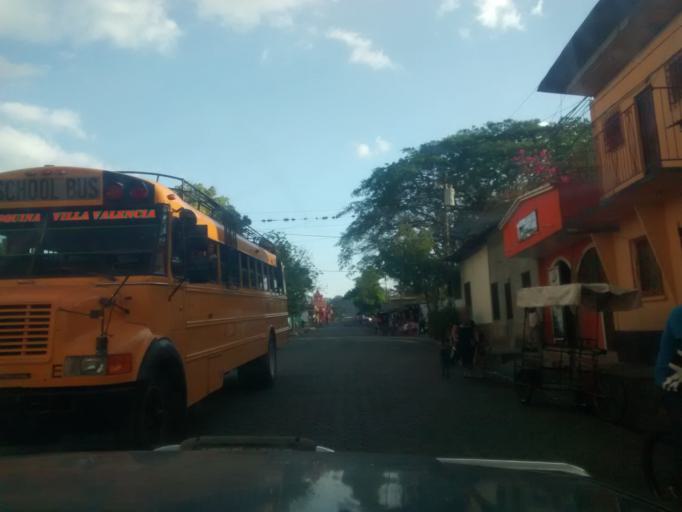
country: NI
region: Jinotega
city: Jinotega
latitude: 13.0900
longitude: -85.9992
